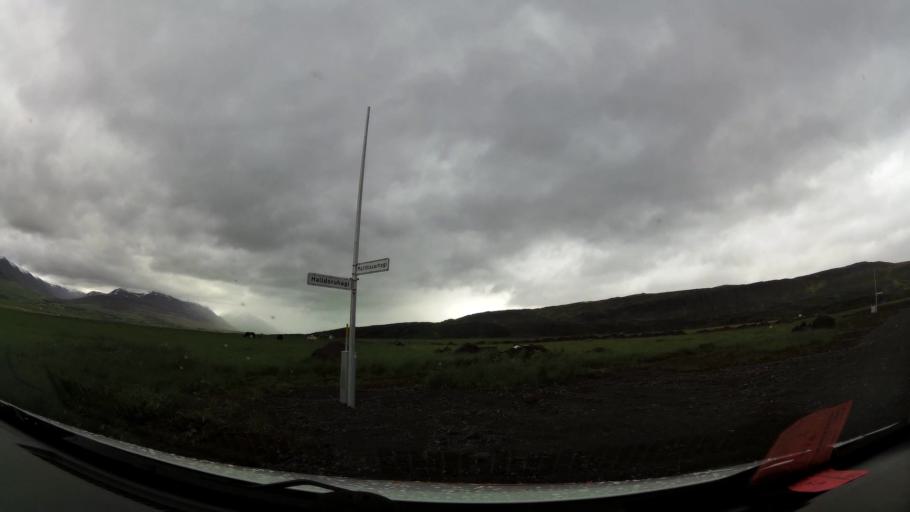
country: IS
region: Northeast
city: Akureyri
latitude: 65.6582
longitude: -18.0919
